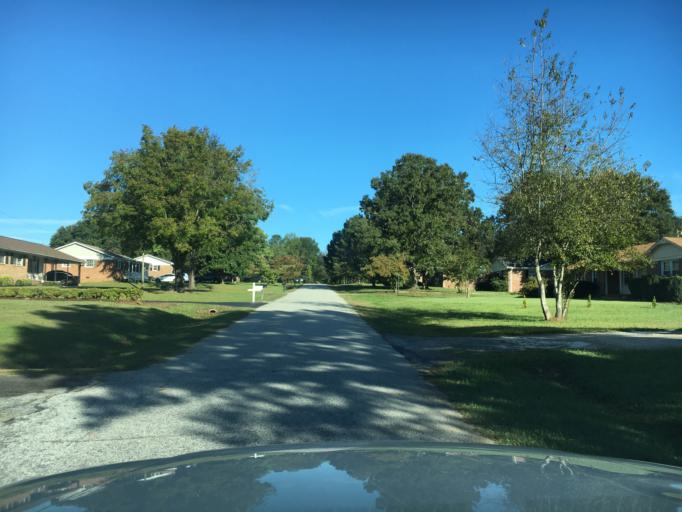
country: US
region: South Carolina
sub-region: Spartanburg County
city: Lyman
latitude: 34.9246
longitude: -82.1222
